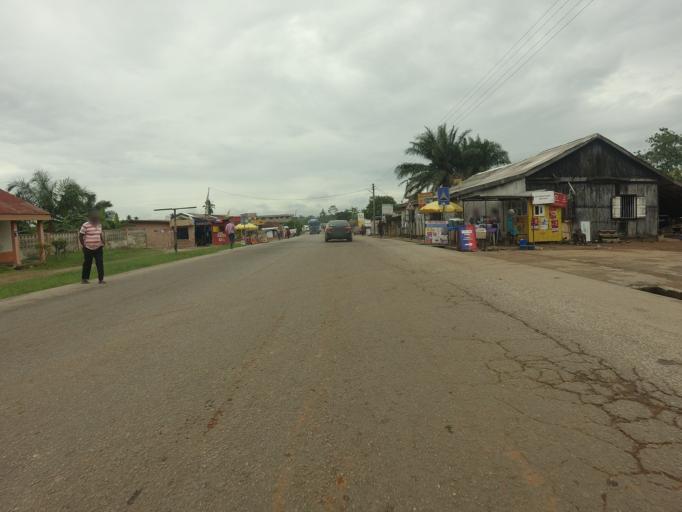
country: GH
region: Eastern
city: Begoro
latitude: 6.3829
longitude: -0.5506
